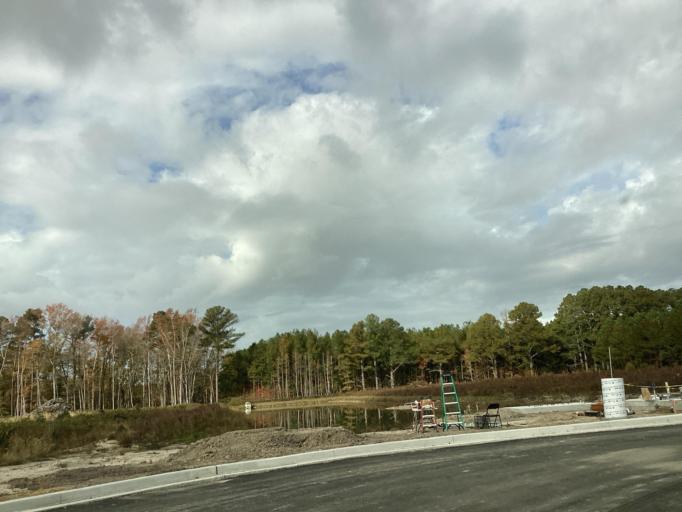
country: US
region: Maryland
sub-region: Somerset County
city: Princess Anne
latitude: 38.2187
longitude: -75.6999
